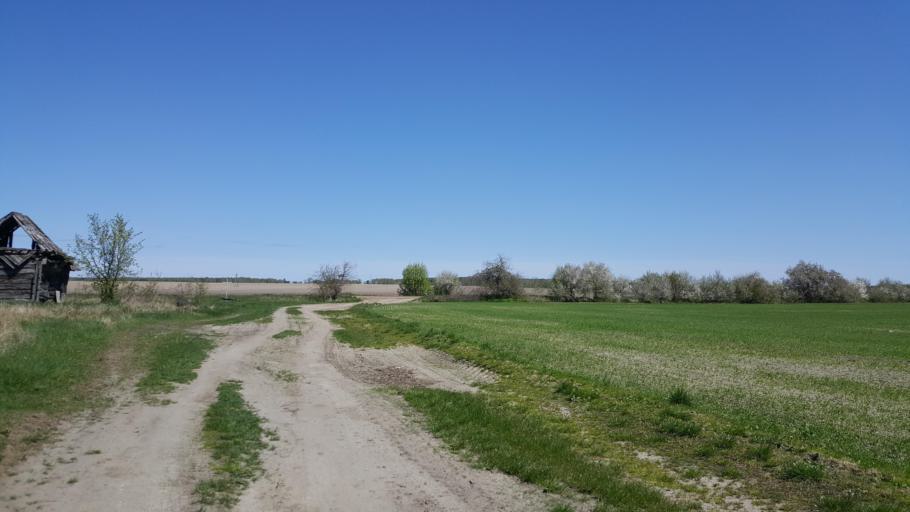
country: BY
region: Brest
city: Kamyanyets
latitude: 52.3276
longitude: 23.7613
